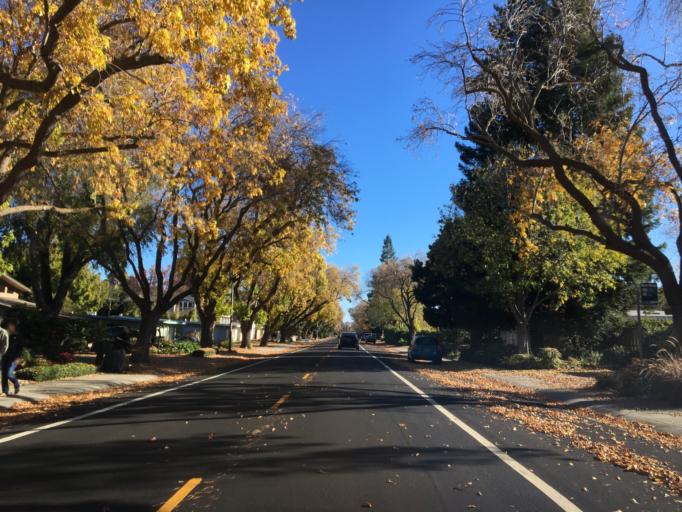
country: US
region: California
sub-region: Santa Clara County
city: Palo Alto
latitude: 37.4295
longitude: -122.1107
